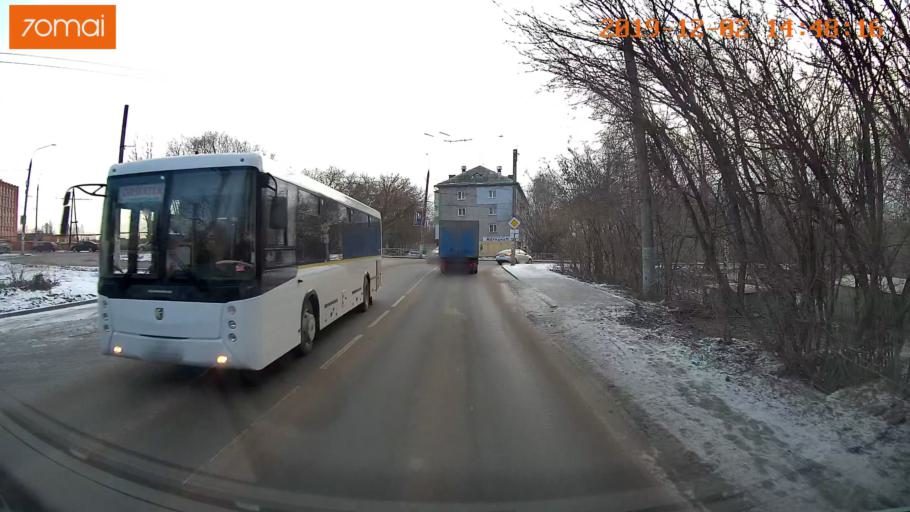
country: RU
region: Ivanovo
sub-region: Gorod Ivanovo
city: Ivanovo
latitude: 56.9851
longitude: 41.0177
